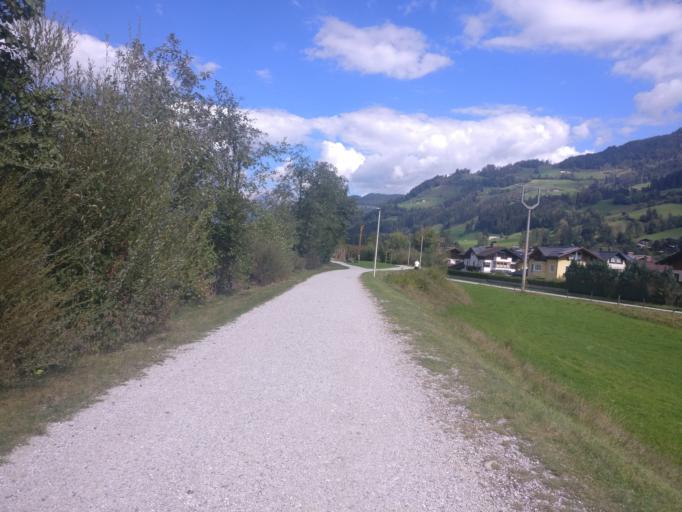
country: AT
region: Salzburg
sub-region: Politischer Bezirk Sankt Johann im Pongau
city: Sankt Johann im Pongau
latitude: 47.3673
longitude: 13.2093
